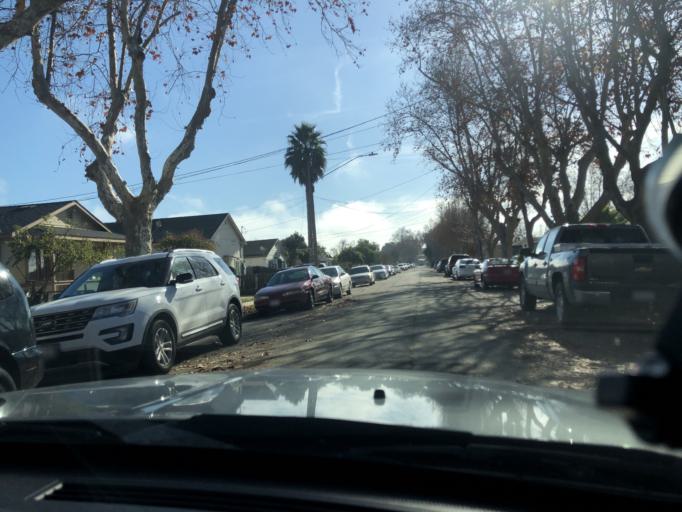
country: US
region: California
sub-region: Monterey County
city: King City
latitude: 36.2089
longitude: -121.1302
